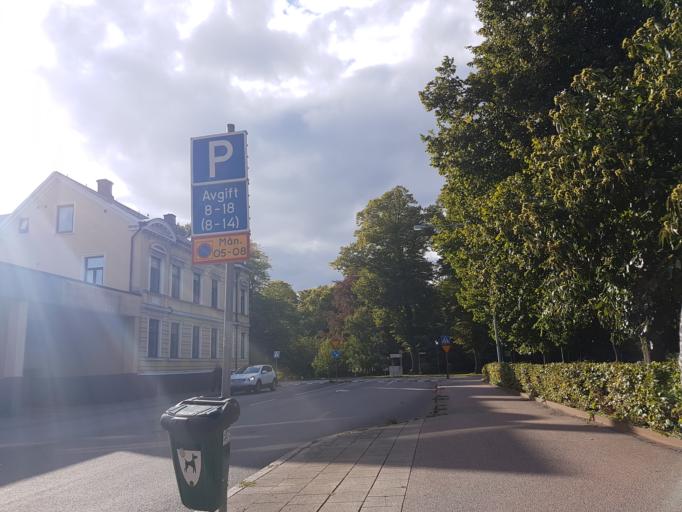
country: SE
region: Skane
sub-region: Landskrona
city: Landskrona
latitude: 55.8721
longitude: 12.8314
